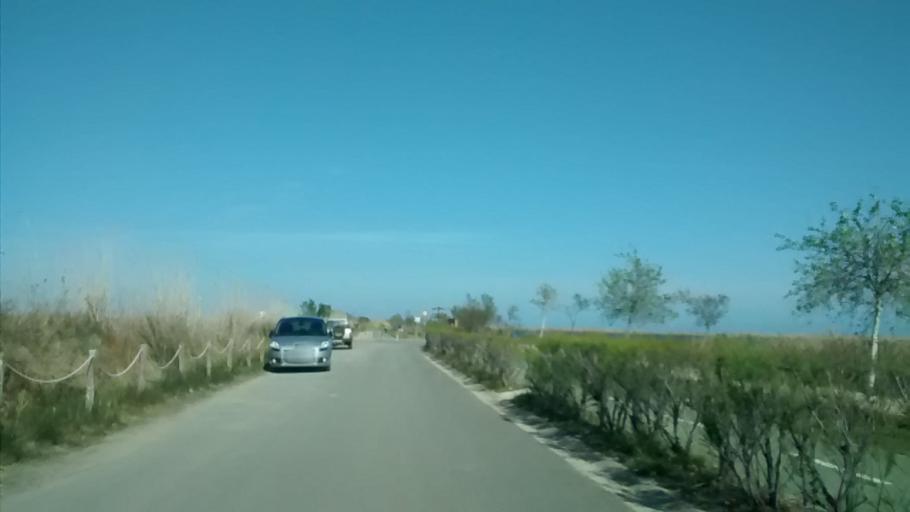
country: ES
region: Catalonia
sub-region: Provincia de Tarragona
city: Deltebre
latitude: 40.7196
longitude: 0.8550
